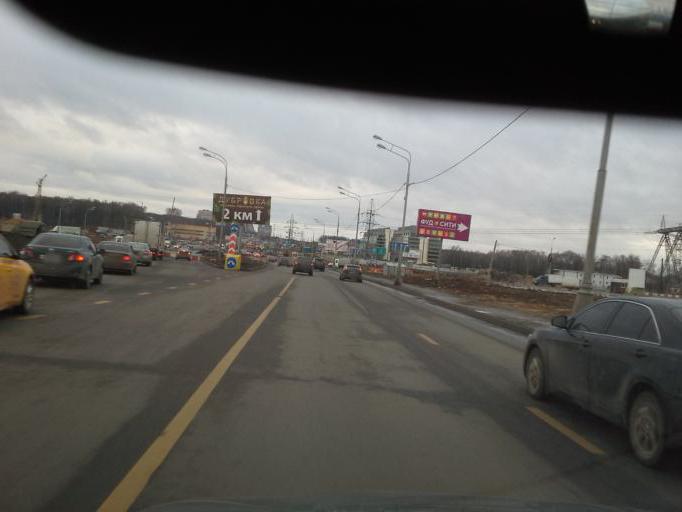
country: RU
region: Moscow
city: Tyoply Stan
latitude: 55.5970
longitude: 37.4797
